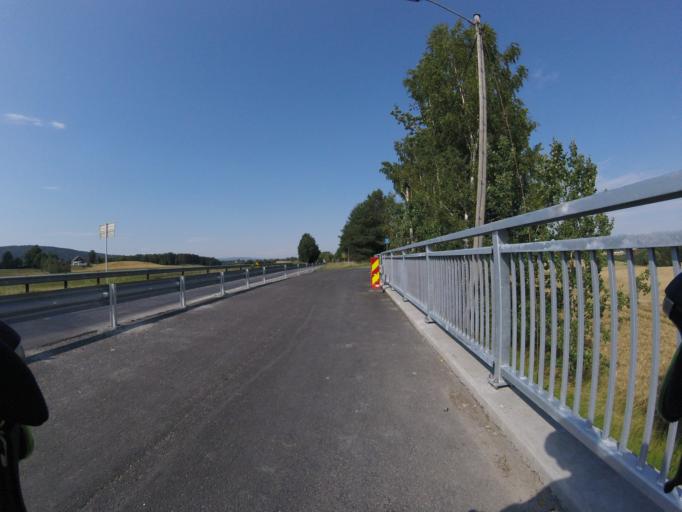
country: NO
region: Akershus
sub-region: Sorum
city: Frogner
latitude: 60.0273
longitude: 11.1159
